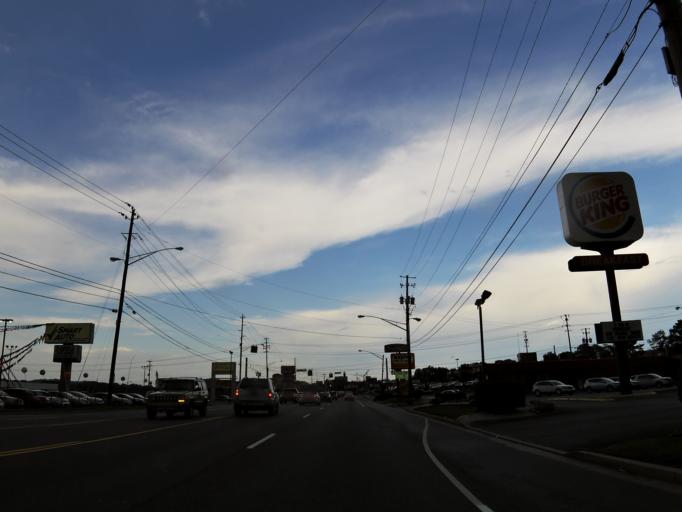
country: US
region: Tennessee
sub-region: Knox County
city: Farragut
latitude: 35.9227
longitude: -84.0603
